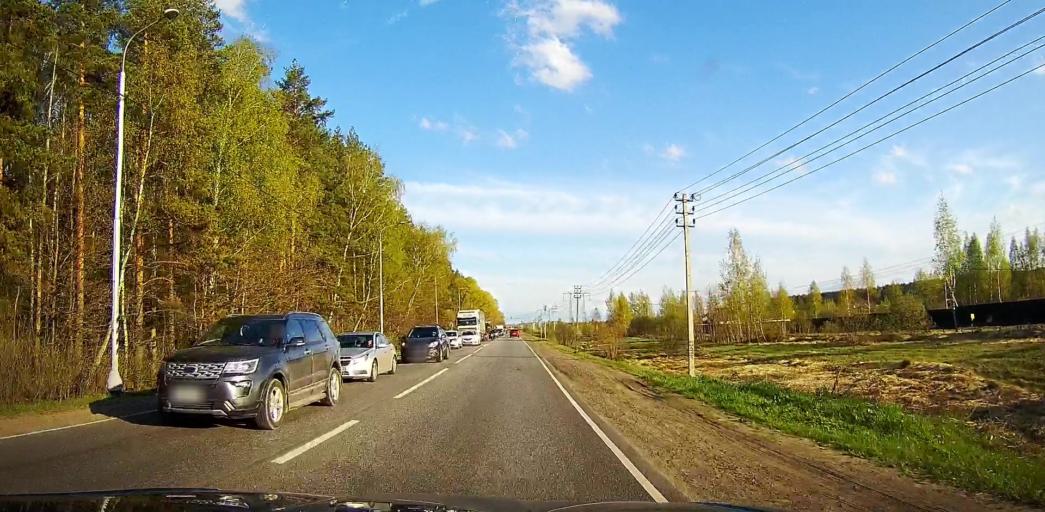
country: RU
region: Moskovskaya
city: Bronnitsy
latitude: 55.3795
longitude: 38.2093
